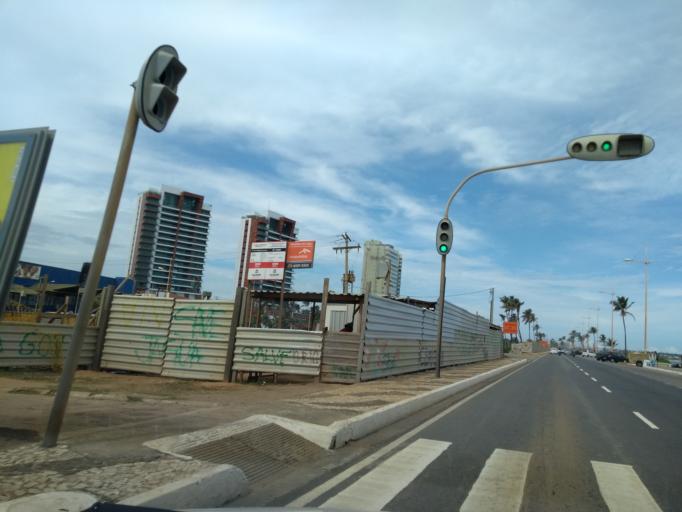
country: BR
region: Bahia
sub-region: Lauro De Freitas
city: Lauro de Freitas
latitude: -12.9608
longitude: -38.3963
